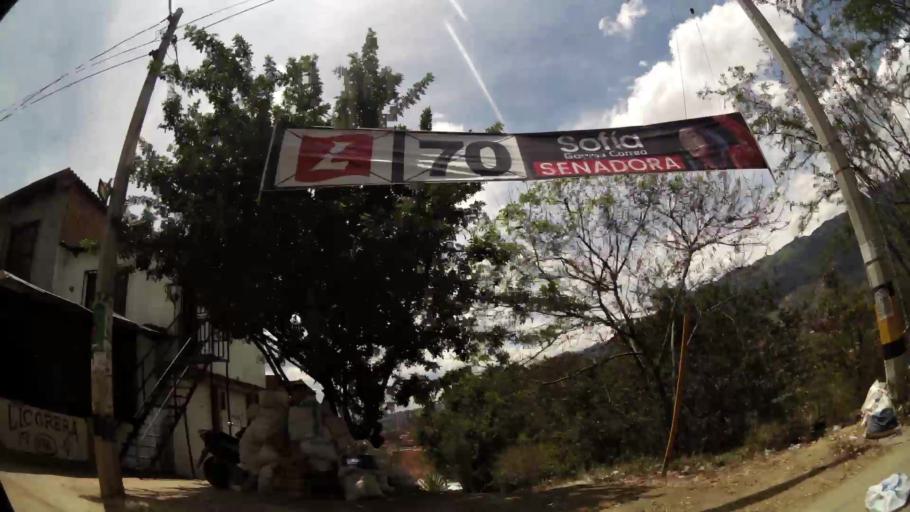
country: CO
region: Antioquia
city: Bello
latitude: 6.3453
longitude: -75.5578
